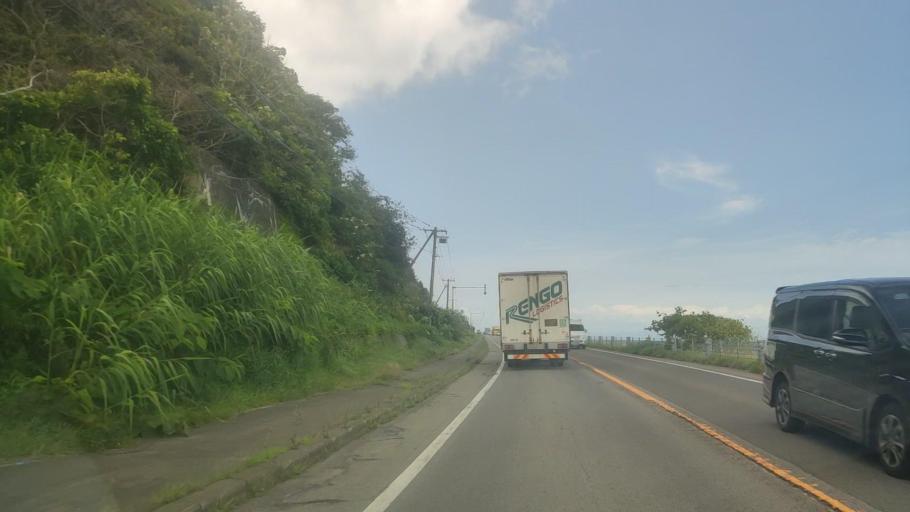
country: JP
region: Hokkaido
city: Nanae
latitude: 42.1470
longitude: 140.4984
